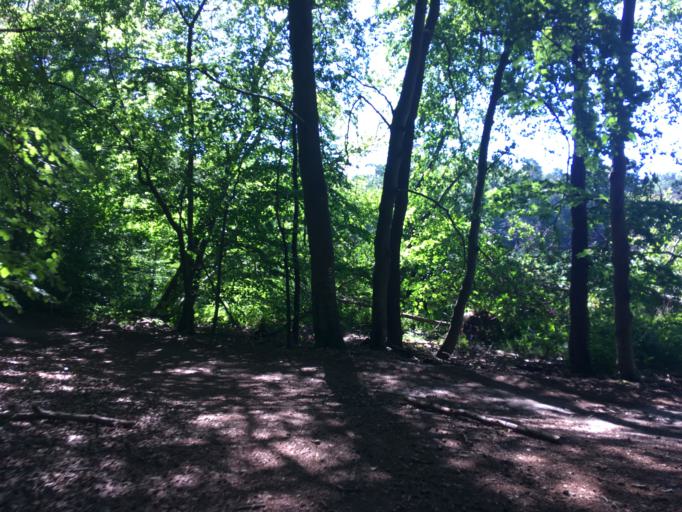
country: DE
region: Brandenburg
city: Furstenberg
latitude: 53.1706
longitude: 13.0371
